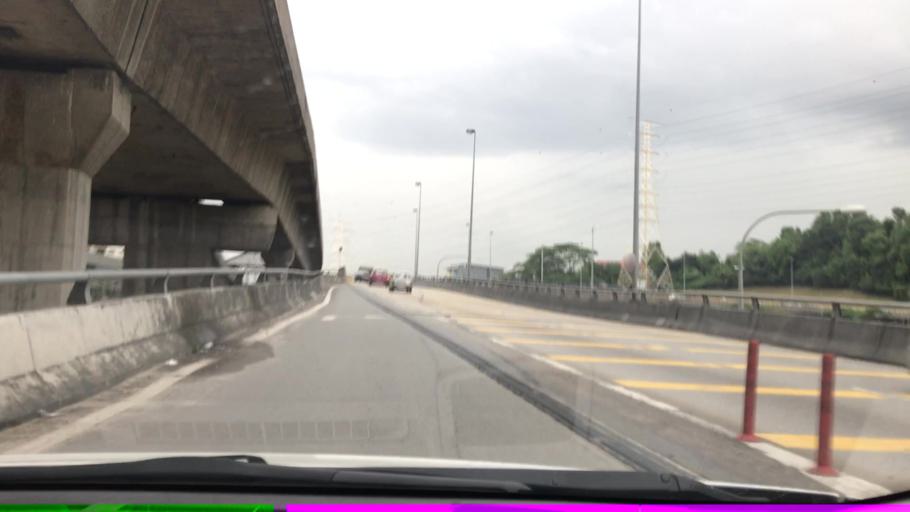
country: MY
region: Kuala Lumpur
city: Kuala Lumpur
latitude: 3.1148
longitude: 101.6638
